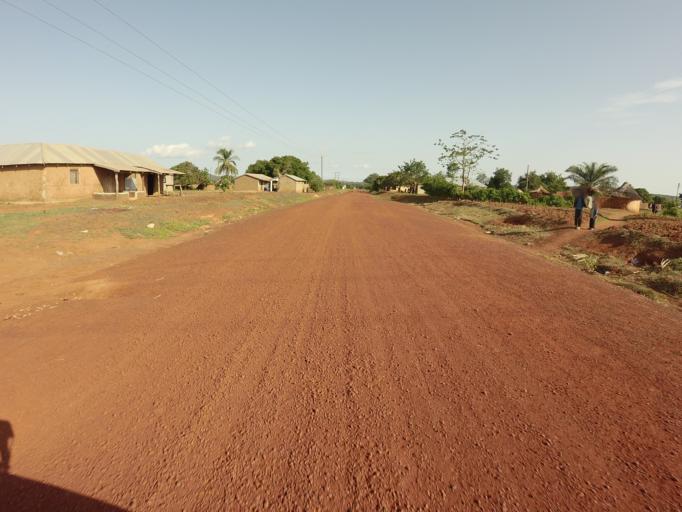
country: GH
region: Upper East
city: Bawku
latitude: 10.6271
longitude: -0.1795
